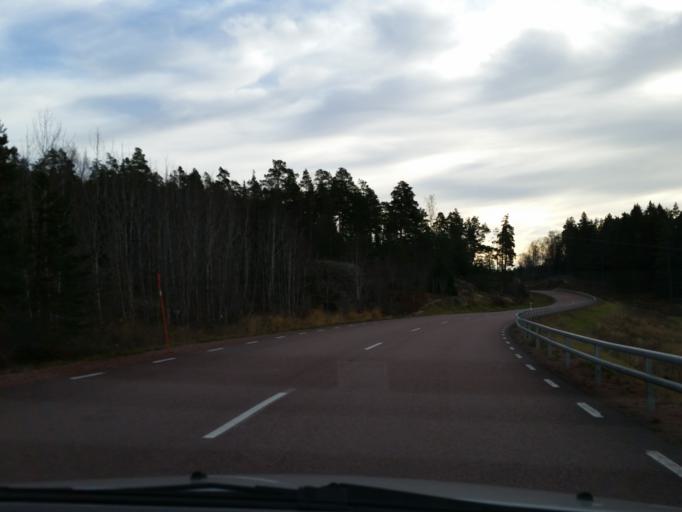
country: AX
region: Alands landsbygd
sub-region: Saltvik
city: Saltvik
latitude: 60.2504
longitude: 20.0392
